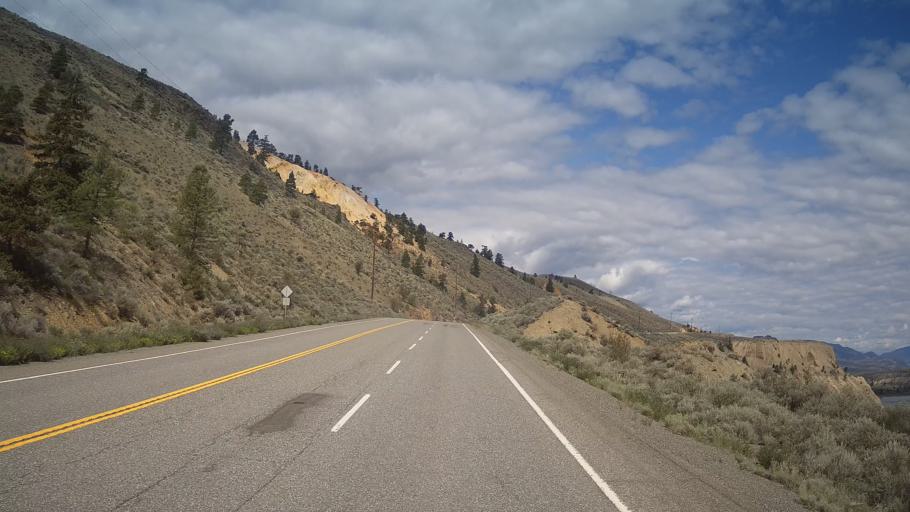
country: CA
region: British Columbia
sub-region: Thompson-Nicola Regional District
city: Ashcroft
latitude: 50.5534
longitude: -121.2982
